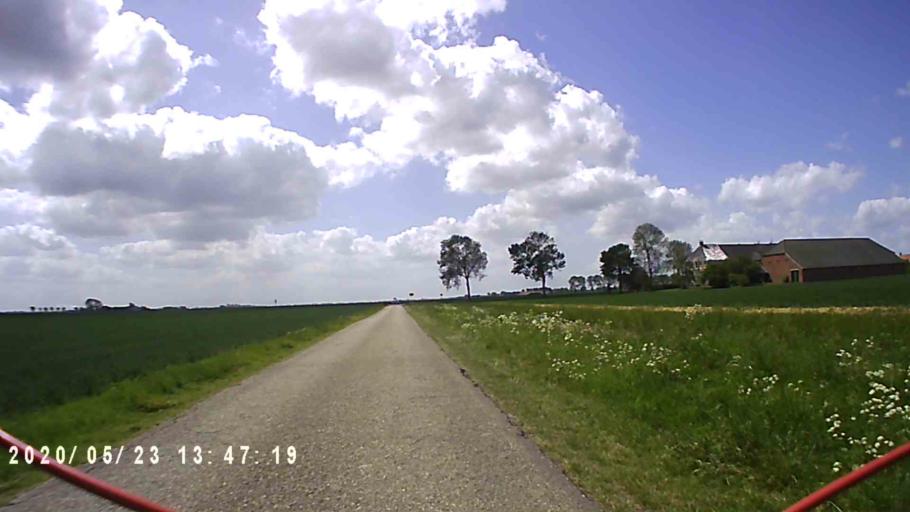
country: NL
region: Groningen
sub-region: Gemeente  Oldambt
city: Winschoten
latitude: 53.2620
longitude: 7.0556
